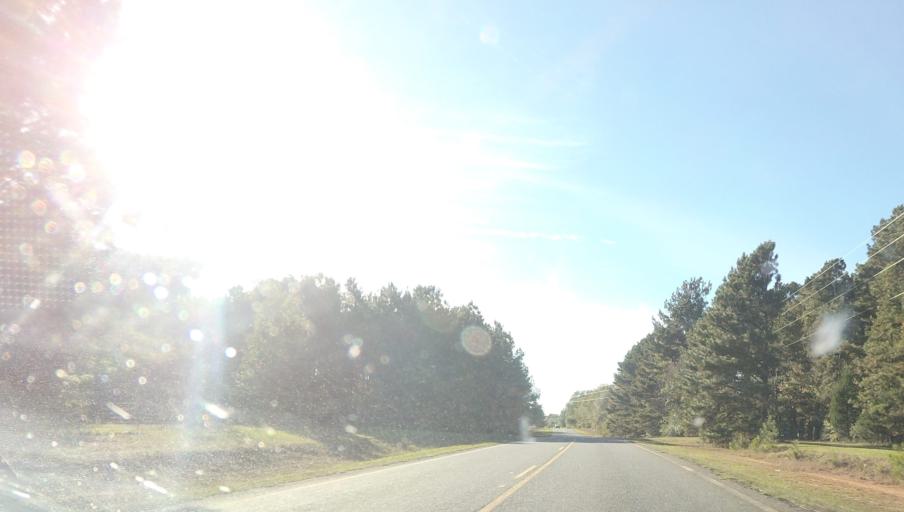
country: US
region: Georgia
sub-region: Talbot County
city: Sardis
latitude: 32.6902
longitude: -84.6853
